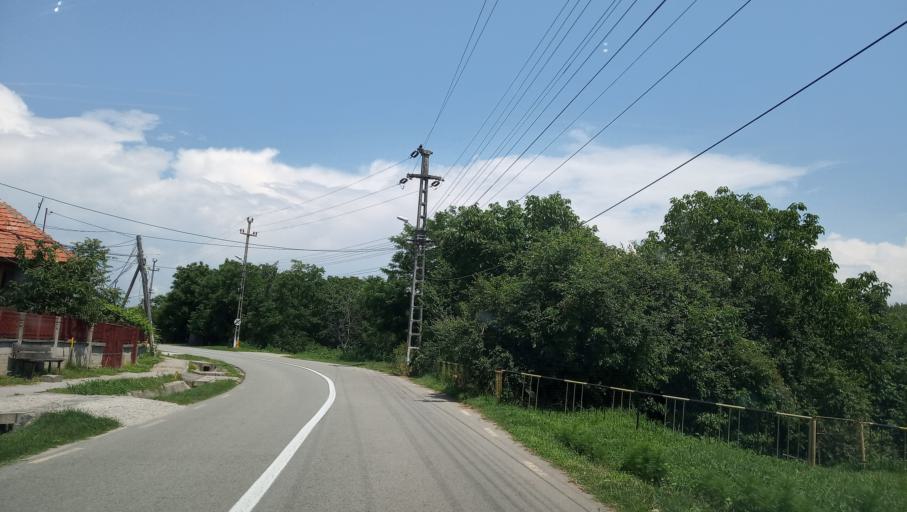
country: RO
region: Gorj
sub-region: Comuna Turcinesti
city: Turcinesti
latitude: 45.0521
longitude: 23.3471
